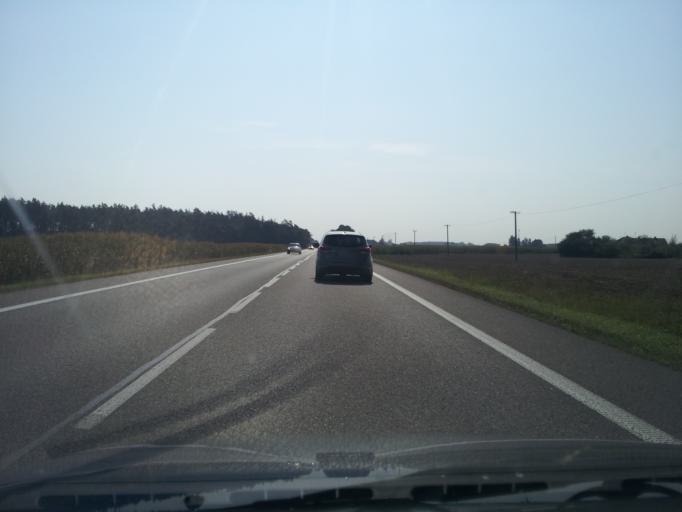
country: PL
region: Masovian Voivodeship
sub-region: Powiat plocki
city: Starozreby
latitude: 52.6633
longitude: 20.0762
